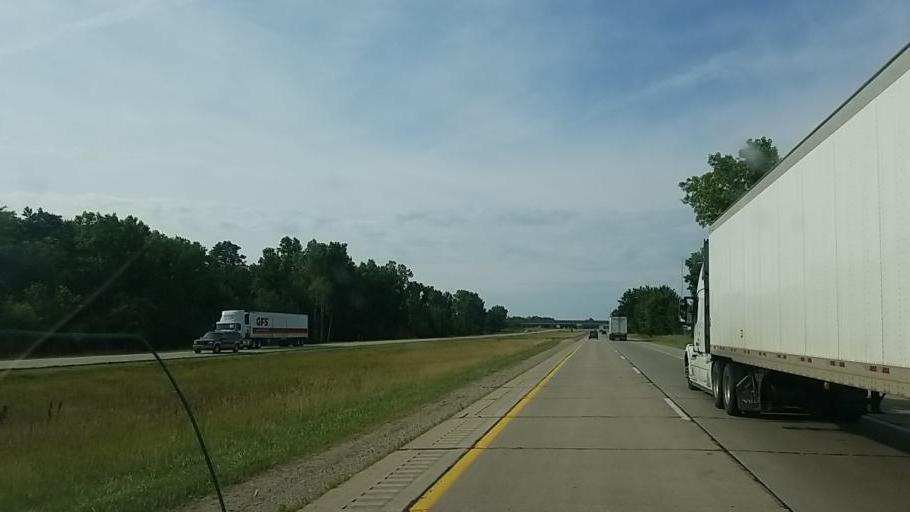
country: US
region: Michigan
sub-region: Eaton County
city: Charlotte
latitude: 42.5435
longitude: -84.8212
